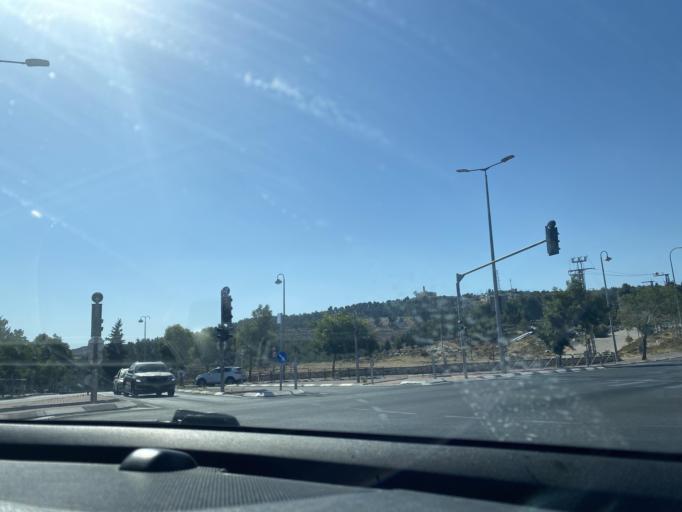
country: PS
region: West Bank
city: Bayt Iksa
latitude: 31.8258
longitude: 35.1887
